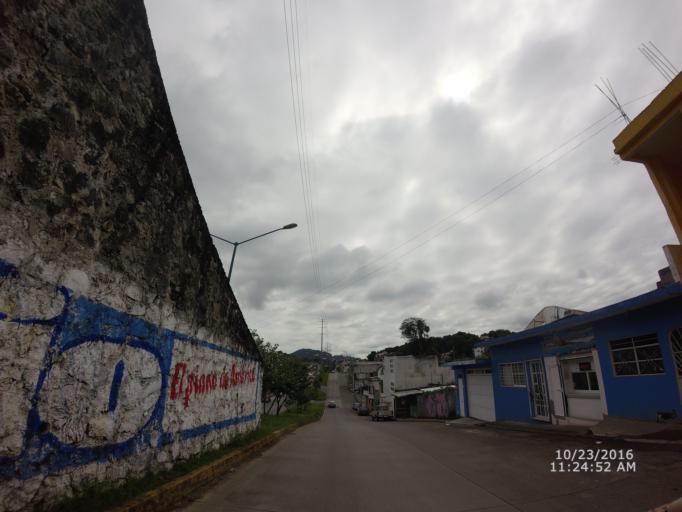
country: MX
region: Veracruz
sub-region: Tlalnelhuayocan
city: Guadalupe Victoria
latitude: 19.5516
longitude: -96.9478
